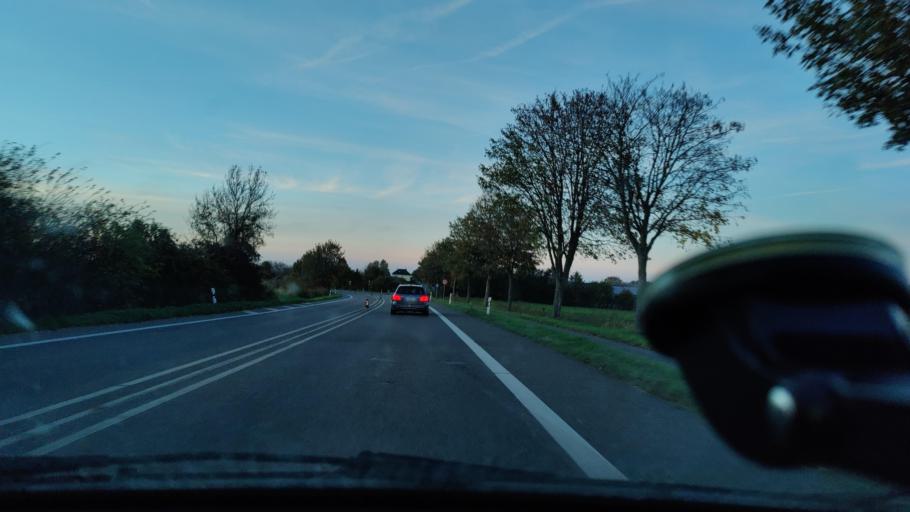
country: DE
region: North Rhine-Westphalia
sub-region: Regierungsbezirk Koln
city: Heinsberg
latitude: 51.0322
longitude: 6.1073
